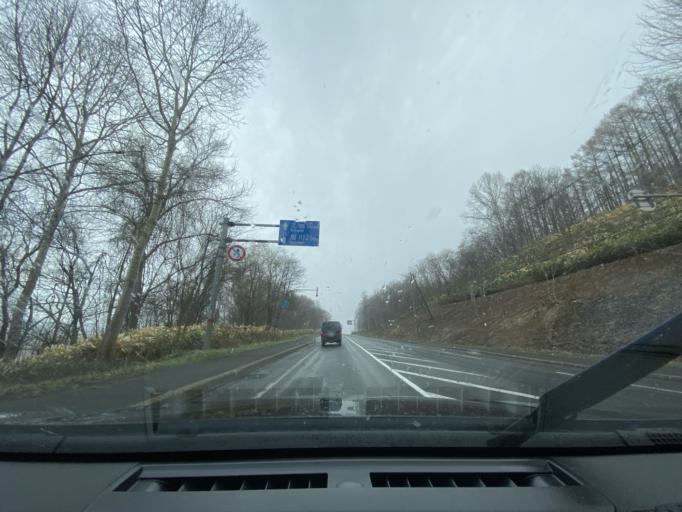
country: JP
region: Hokkaido
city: Fukagawa
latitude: 43.7074
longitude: 142.1132
